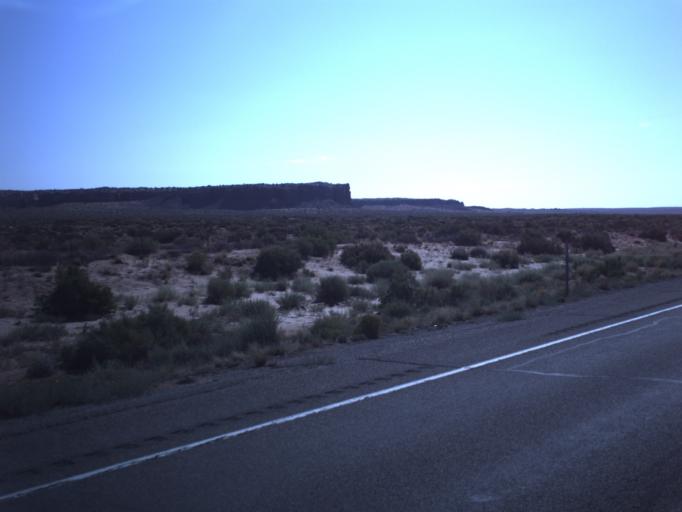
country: US
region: Utah
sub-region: San Juan County
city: Blanding
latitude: 37.1983
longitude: -109.6021
